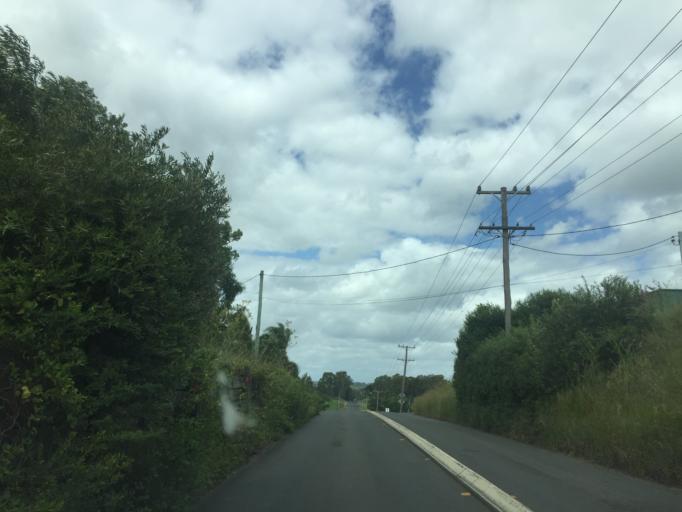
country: AU
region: New South Wales
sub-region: Penrith Municipality
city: Kingswood Park
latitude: -33.7889
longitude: 150.7416
